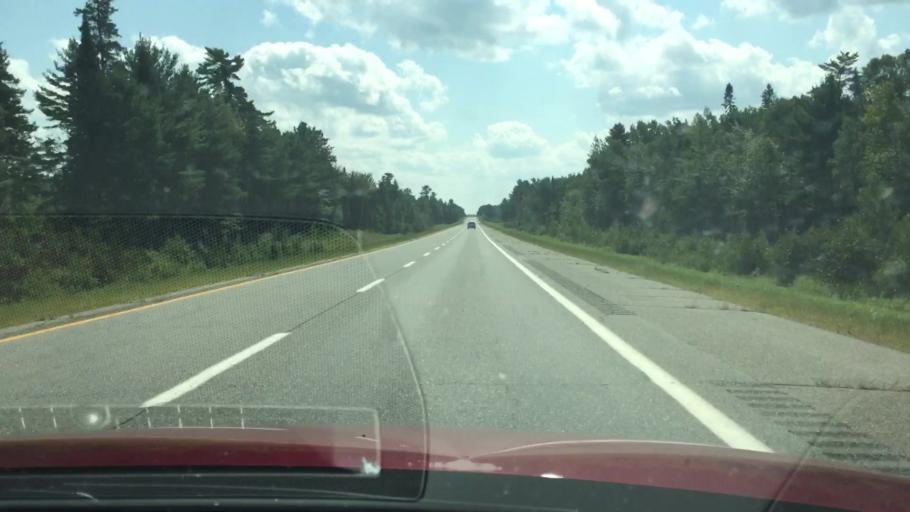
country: US
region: Maine
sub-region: Penobscot County
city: Lincoln
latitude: 45.4043
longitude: -68.5979
